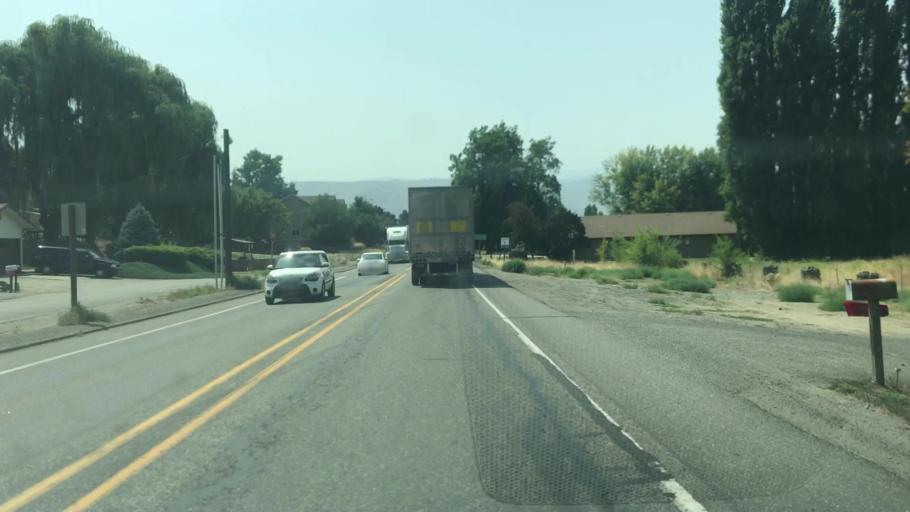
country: US
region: Washington
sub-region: Chelan County
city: Wenatchee
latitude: 47.4302
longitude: -120.2977
